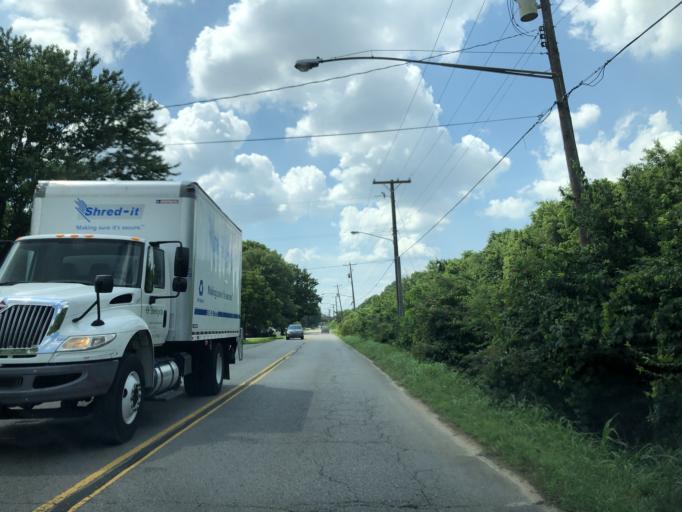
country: US
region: Tennessee
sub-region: Davidson County
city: Oak Hill
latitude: 36.1204
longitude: -86.7314
